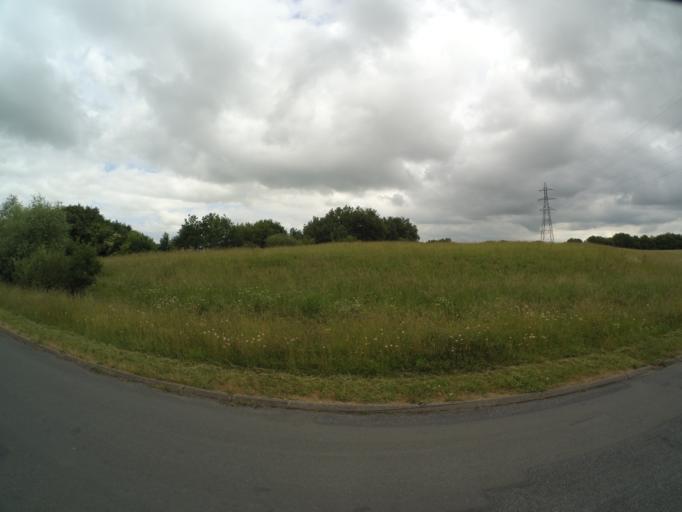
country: FR
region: Poitou-Charentes
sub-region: Departement de la Charente-Maritime
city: Breuil-Magne
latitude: 45.9676
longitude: -0.9788
